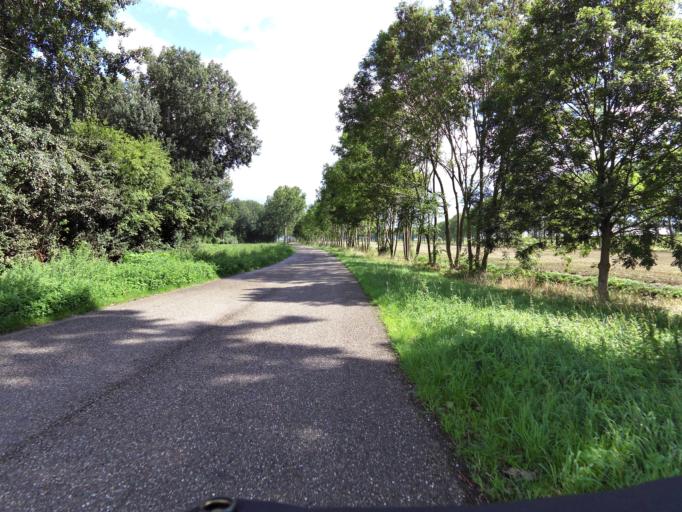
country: NL
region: North Brabant
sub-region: Gemeente Steenbergen
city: Dinteloord
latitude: 51.6609
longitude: 4.2970
